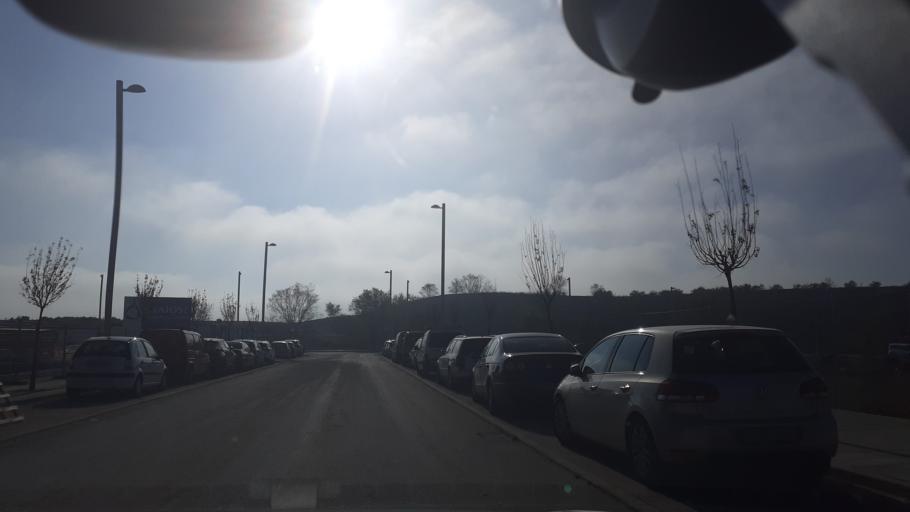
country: ES
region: Madrid
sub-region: Provincia de Madrid
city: Coslada
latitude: 40.3975
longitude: -3.5581
